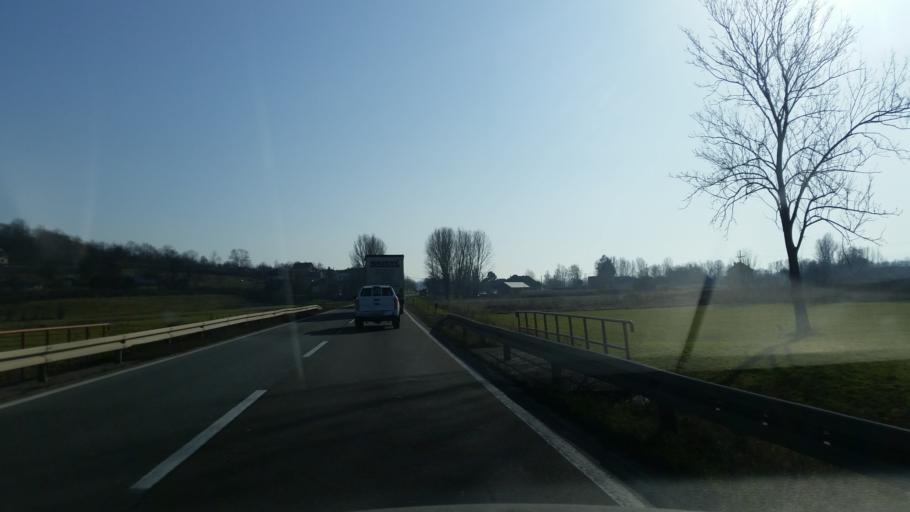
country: RS
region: Central Serbia
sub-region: Kolubarski Okrug
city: Lajkovac
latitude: 44.3399
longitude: 20.2081
